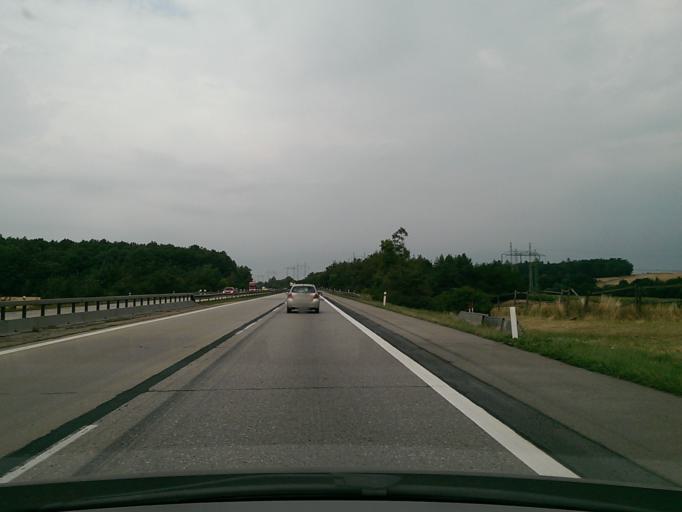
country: CZ
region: South Moravian
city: Ricany
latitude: 49.2402
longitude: 16.3706
